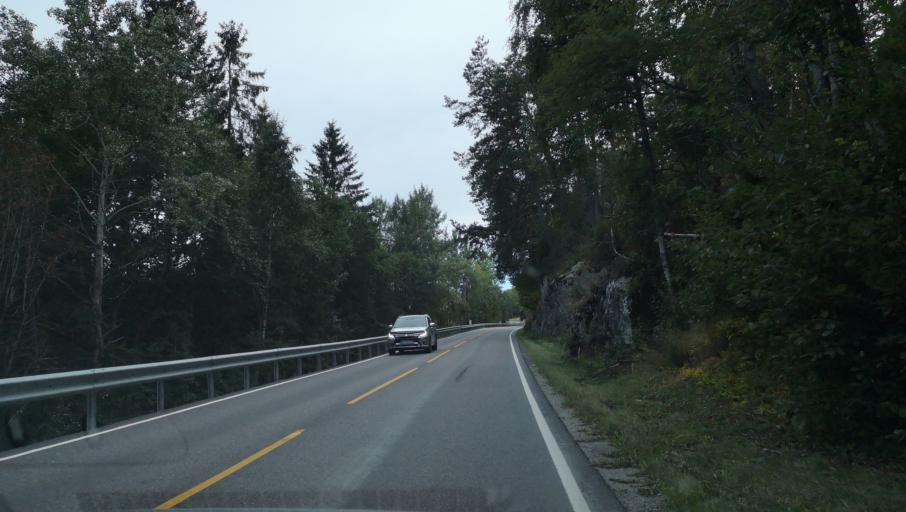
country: NO
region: Ostfold
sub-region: Hobol
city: Tomter
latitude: 59.7179
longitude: 11.0549
